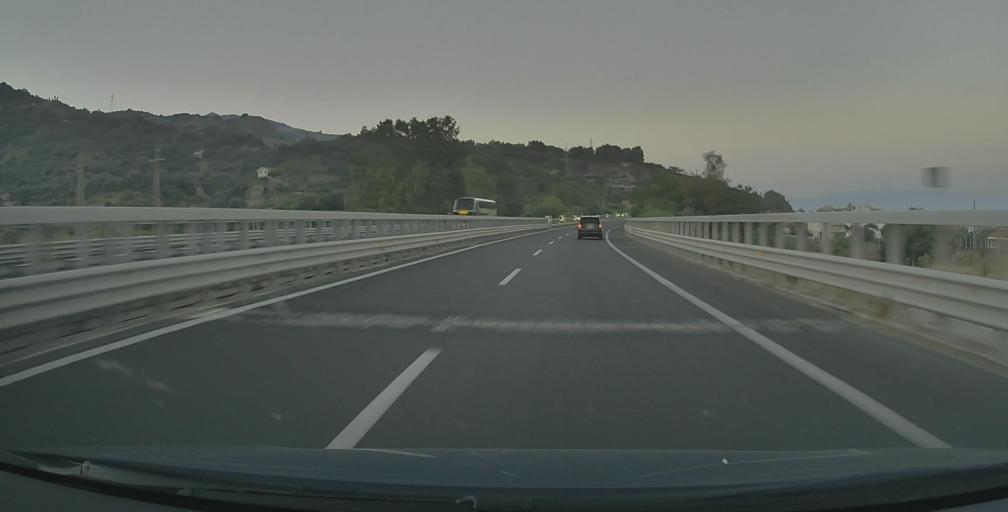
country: IT
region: Sicily
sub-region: Messina
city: Nizza di Sicilia
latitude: 37.9985
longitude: 15.4128
